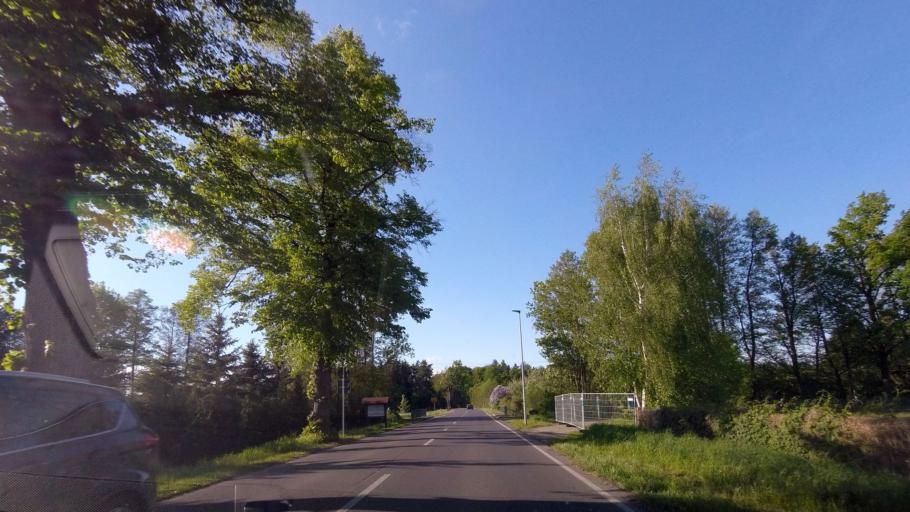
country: DE
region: Brandenburg
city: Luebben
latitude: 51.8900
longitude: 13.9007
